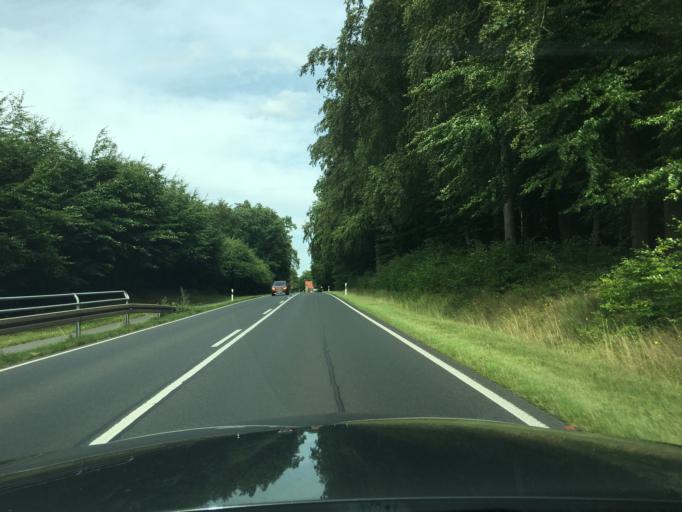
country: DE
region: Mecklenburg-Vorpommern
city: Neustrelitz
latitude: 53.3905
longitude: 13.0954
